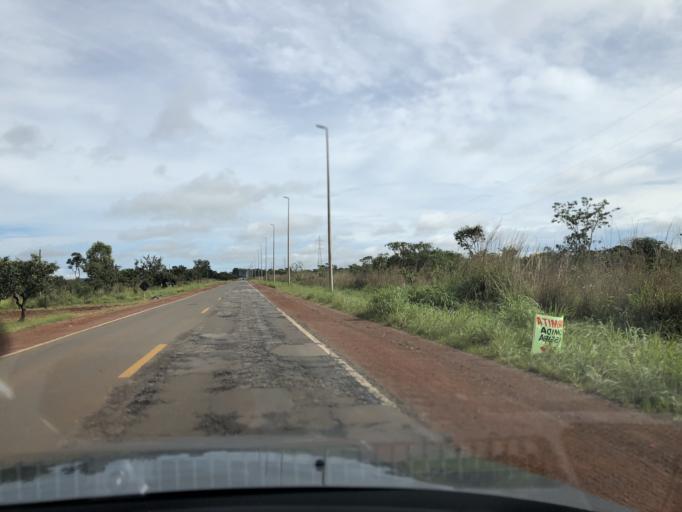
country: BR
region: Federal District
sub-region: Brasilia
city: Brasilia
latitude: -15.6928
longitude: -48.0888
